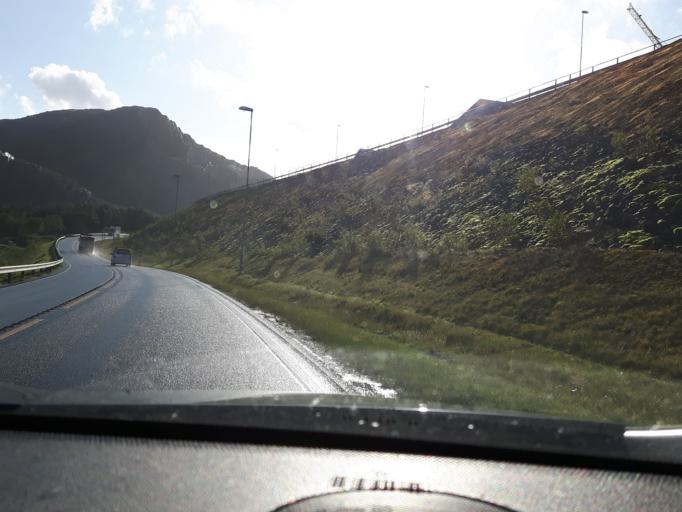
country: NO
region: Rogaland
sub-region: Gjesdal
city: Algard
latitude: 58.7541
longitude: 5.9111
